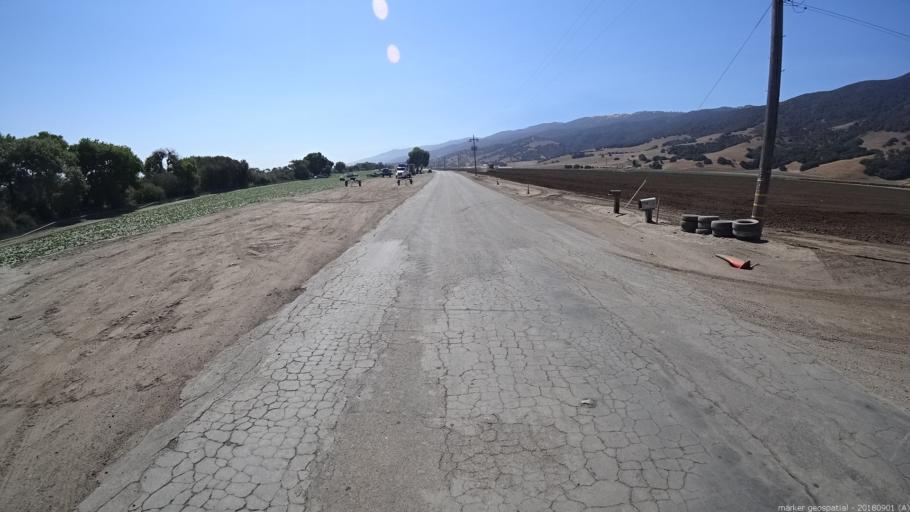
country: US
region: California
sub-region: Monterey County
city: Chualar
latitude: 36.5473
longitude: -121.5462
